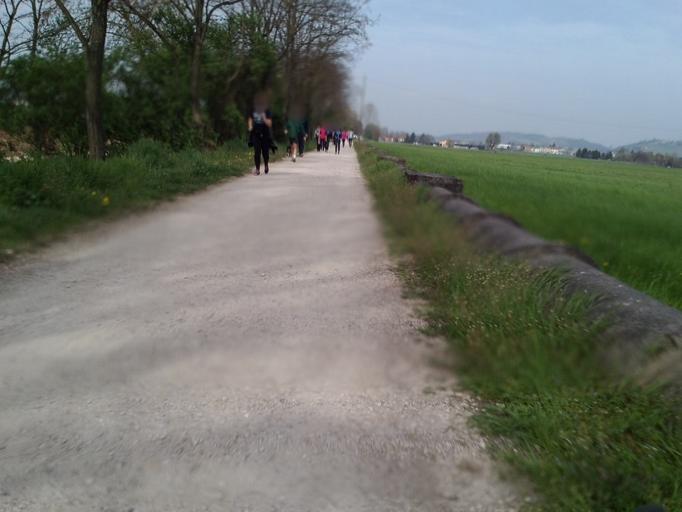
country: IT
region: Veneto
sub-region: Provincia di Verona
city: Rosegaferro
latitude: 45.3539
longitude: 10.8217
